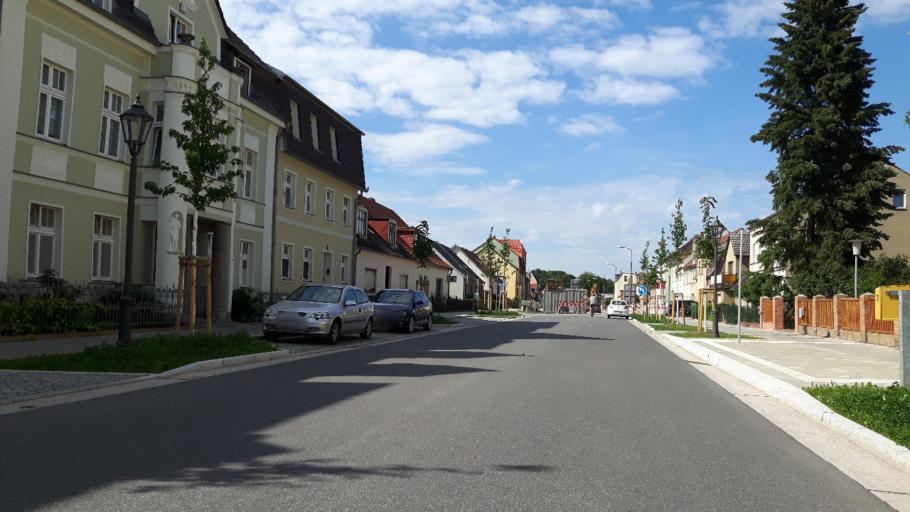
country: DE
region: Brandenburg
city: Beelitz
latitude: 52.2380
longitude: 12.9789
